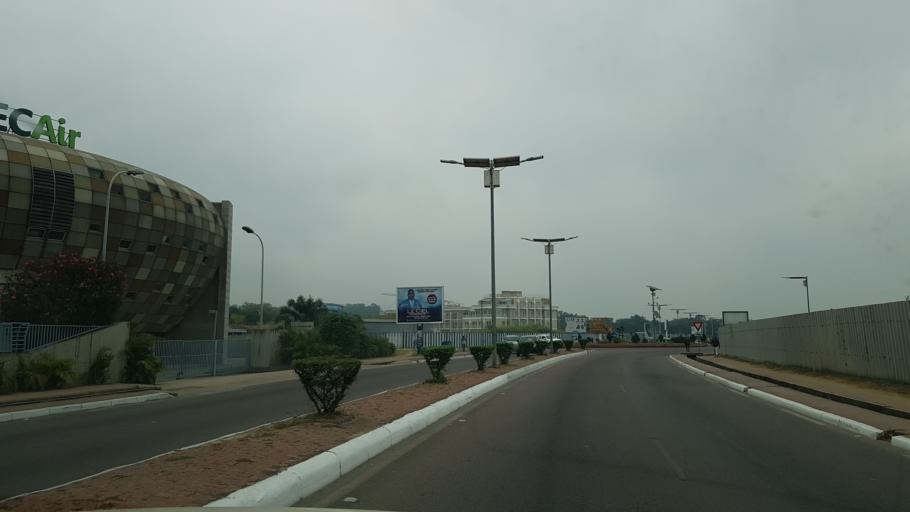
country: CG
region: Brazzaville
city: Brazzaville
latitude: -4.2591
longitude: 15.2547
